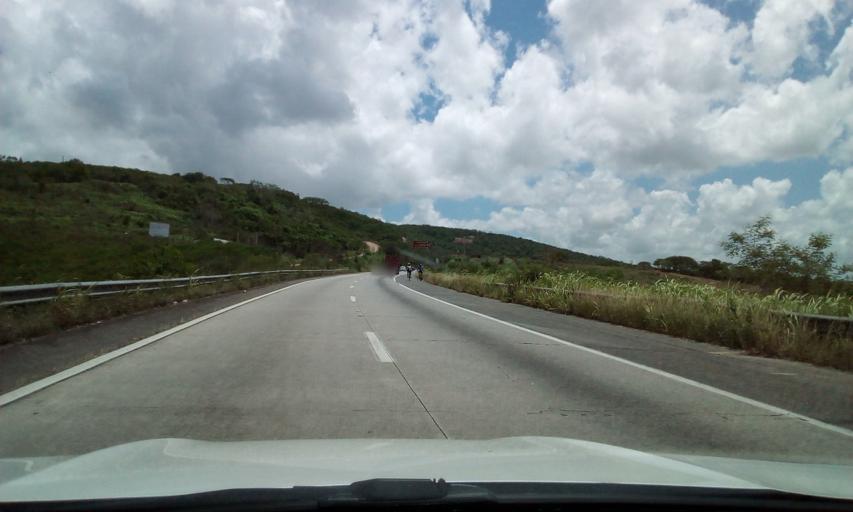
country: BR
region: Pernambuco
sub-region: Cha Grande
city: Cha Grande
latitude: -8.1715
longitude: -35.4787
